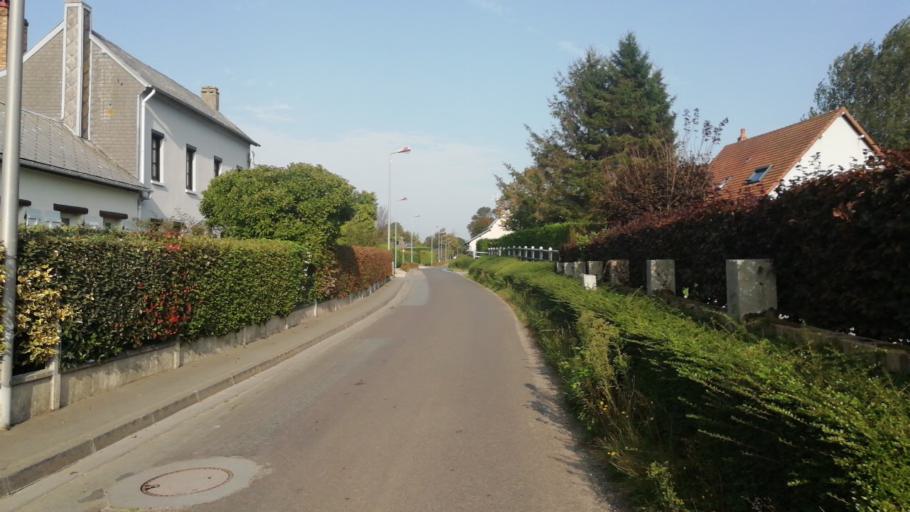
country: FR
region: Haute-Normandie
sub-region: Departement de la Seine-Maritime
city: Saint-Romain-de-Colbosc
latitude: 49.4973
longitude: 0.3668
